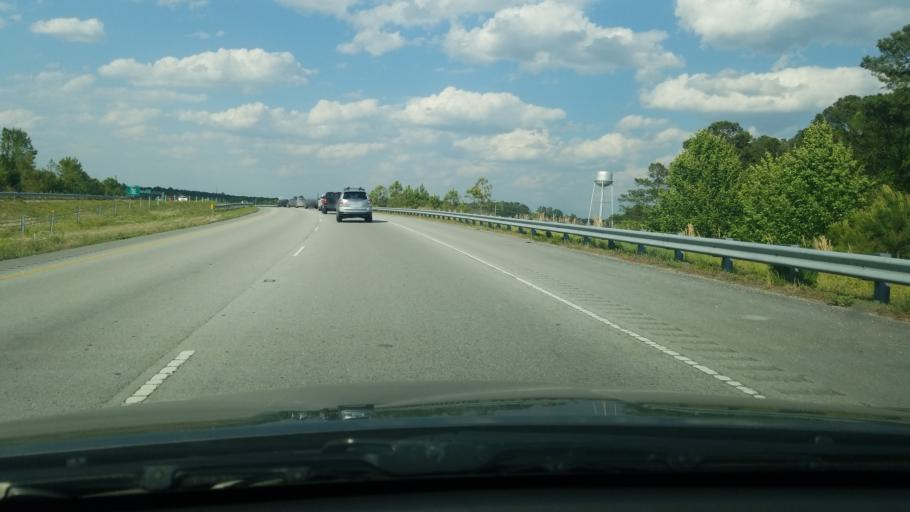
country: US
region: North Carolina
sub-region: Onslow County
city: Jacksonville
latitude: 34.7534
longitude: -77.3963
